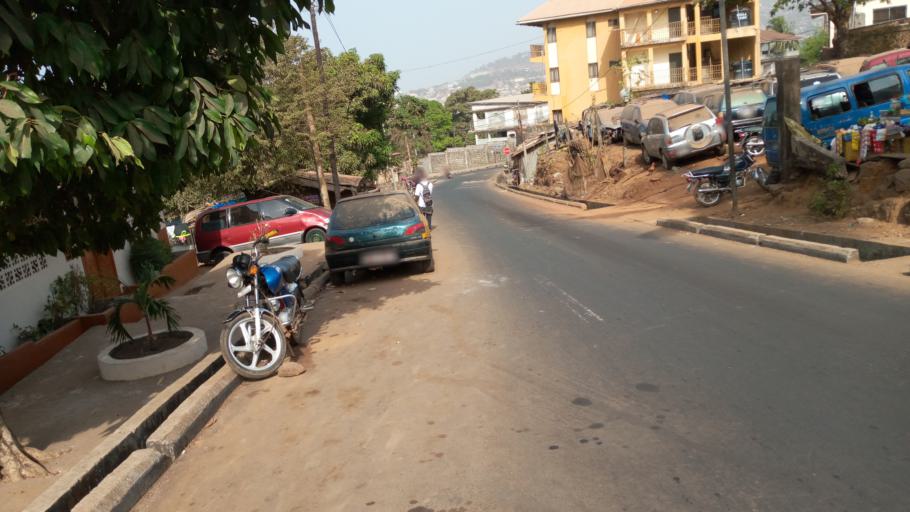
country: SL
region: Western Area
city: Freetown
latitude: 8.4800
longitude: -13.2598
